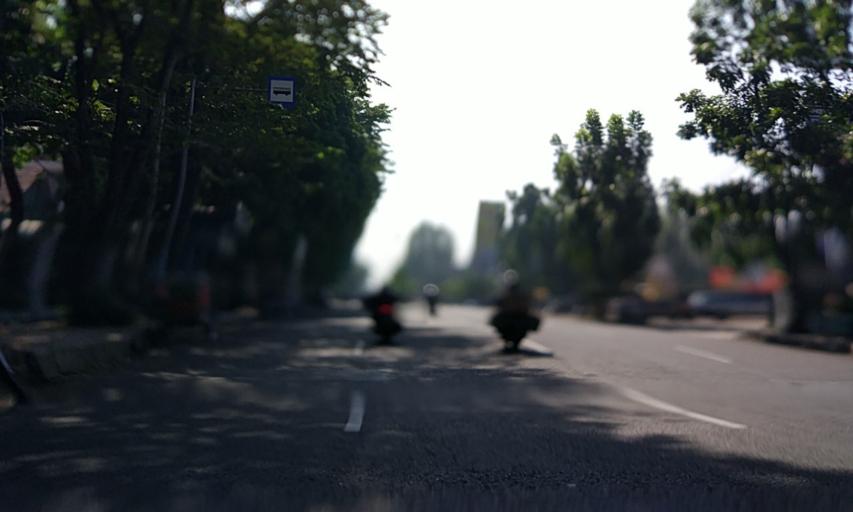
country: ID
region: West Java
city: Bandung
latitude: -6.9166
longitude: 107.6284
